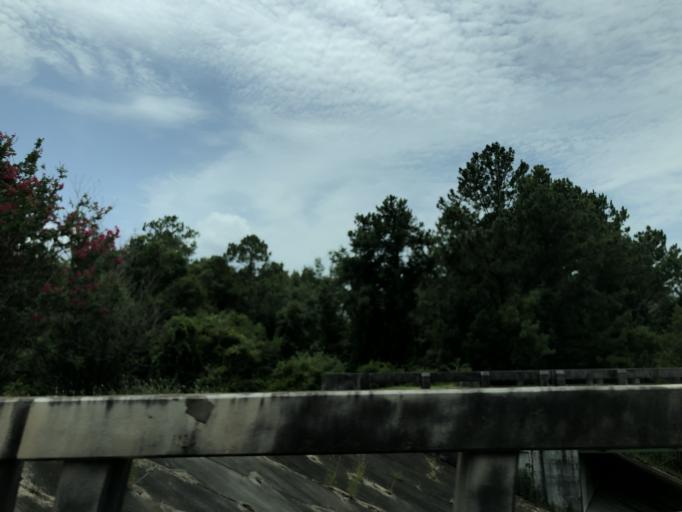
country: US
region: Georgia
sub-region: Bulloch County
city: Brooklet
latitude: 32.2714
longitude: -81.7483
